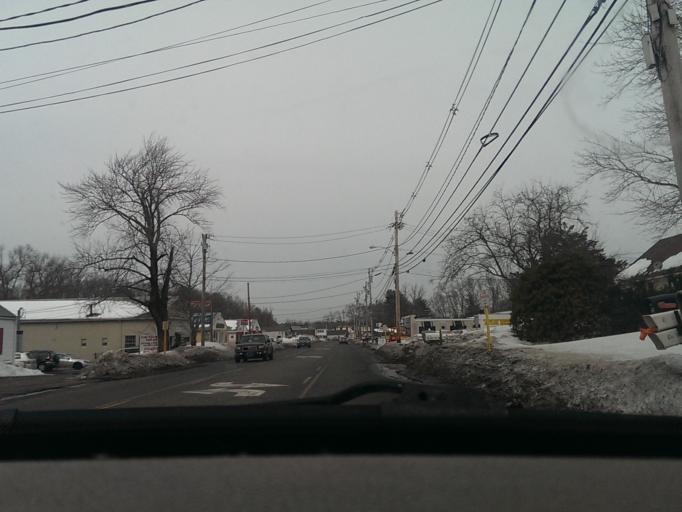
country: US
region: Massachusetts
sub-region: Hampden County
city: East Longmeadow
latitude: 42.0556
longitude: -72.5182
